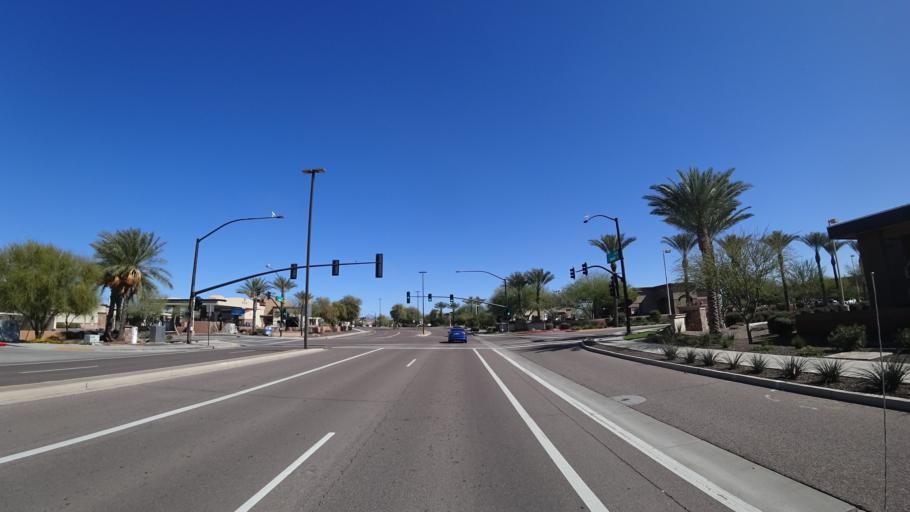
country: US
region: Arizona
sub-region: Maricopa County
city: Gilbert
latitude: 33.2977
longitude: -111.7472
